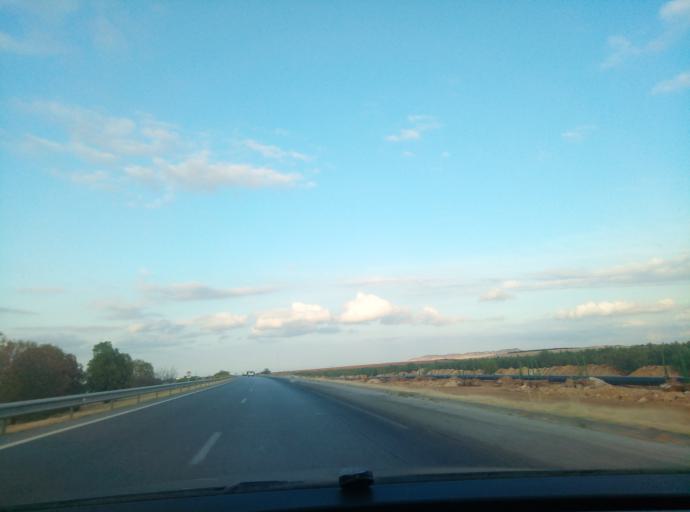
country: TN
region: Manouba
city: El Battan
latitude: 36.6594
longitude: 9.8391
